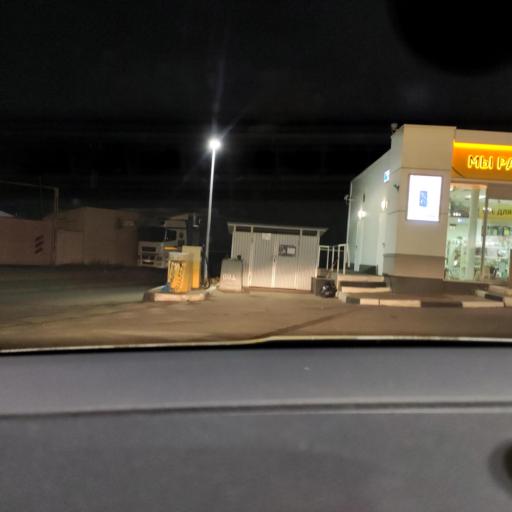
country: RU
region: Moskovskaya
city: Ivanteyevka
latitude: 55.9609
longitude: 37.9216
